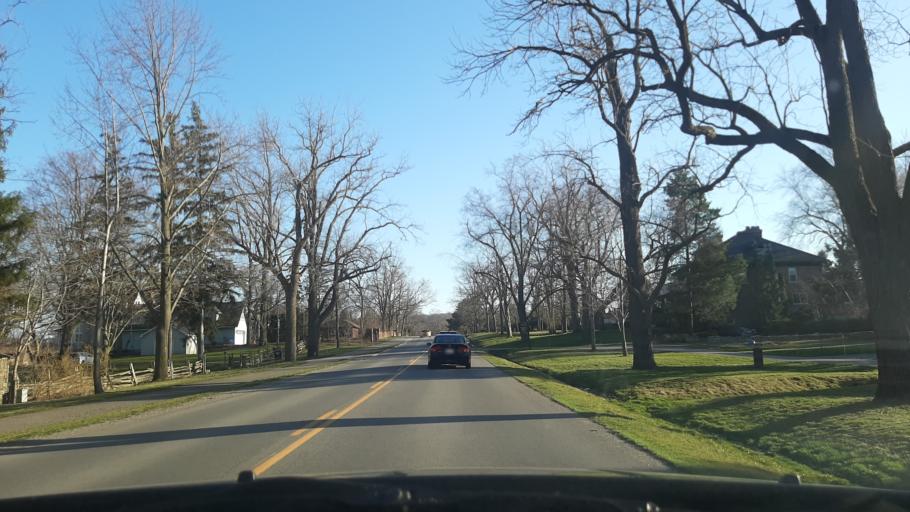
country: US
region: New York
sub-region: Niagara County
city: Lewiston
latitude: 43.1768
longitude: -79.0585
